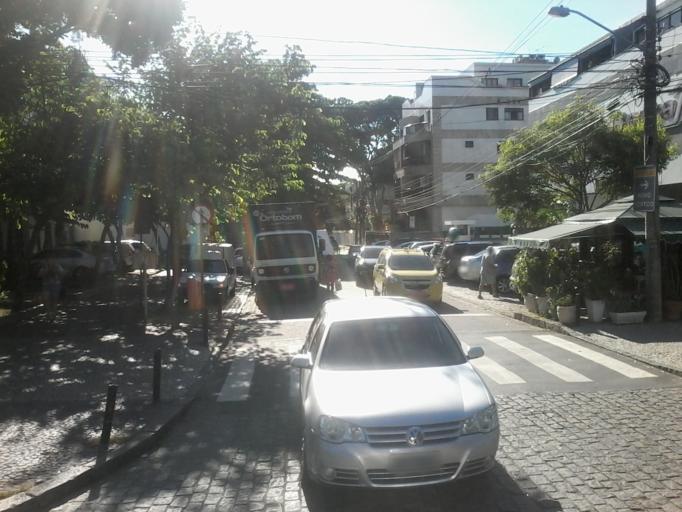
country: BR
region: Rio de Janeiro
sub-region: Rio De Janeiro
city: Rio de Janeiro
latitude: -23.0112
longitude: -43.3049
